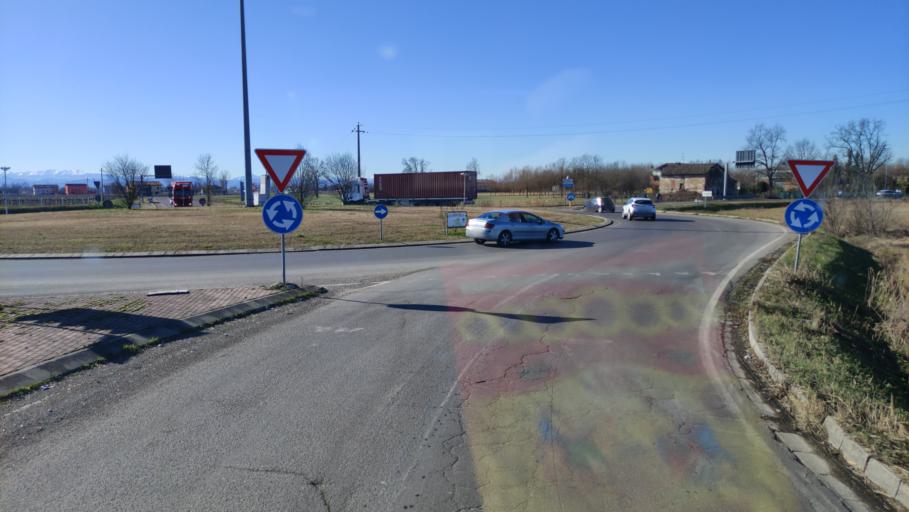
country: IT
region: Emilia-Romagna
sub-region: Provincia di Reggio Emilia
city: Correggio
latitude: 44.7507
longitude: 10.7863
